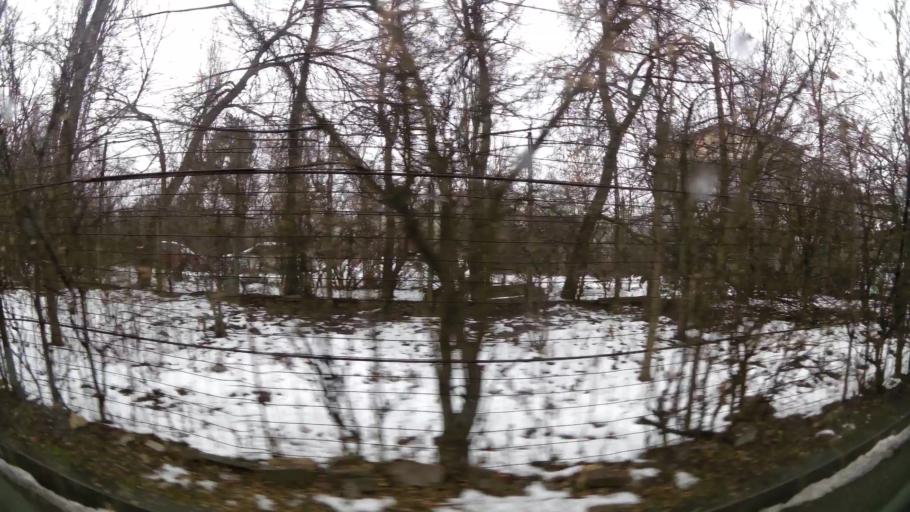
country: RO
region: Ilfov
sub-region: Comuna Chiajna
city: Rosu
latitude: 44.4933
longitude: 26.0445
